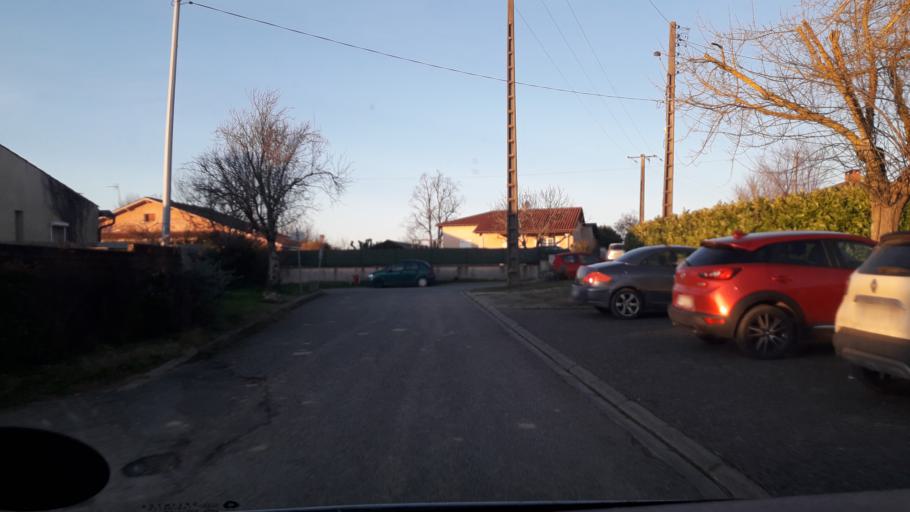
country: FR
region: Midi-Pyrenees
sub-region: Departement du Gers
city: Gimont
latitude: 43.5972
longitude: 0.9833
